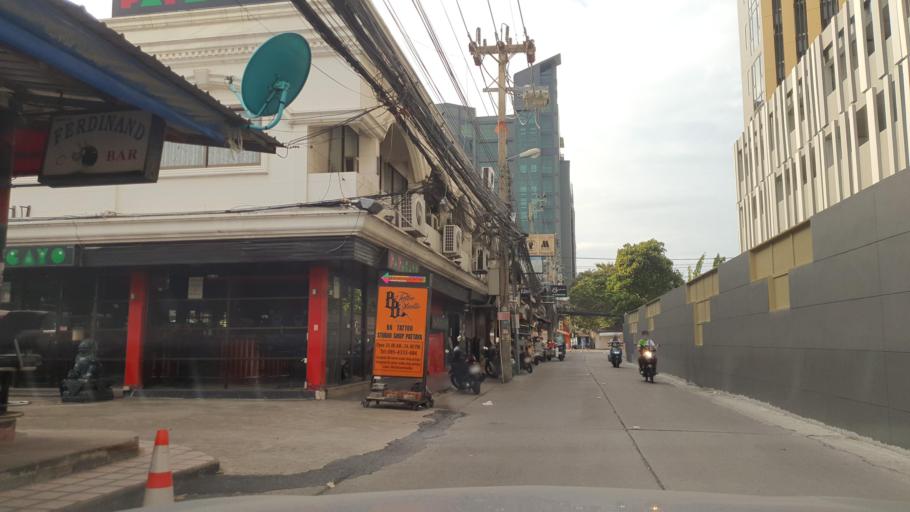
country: TH
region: Chon Buri
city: Phatthaya
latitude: 12.9304
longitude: 100.8828
